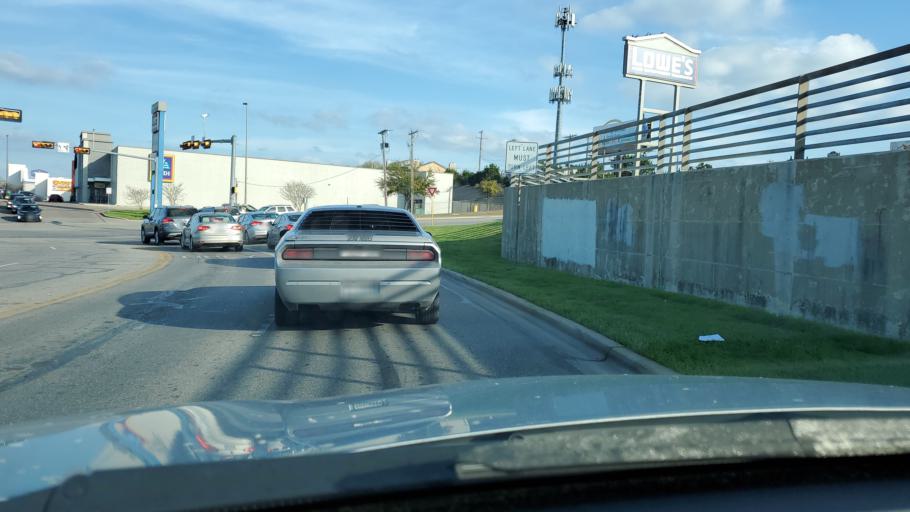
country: US
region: Texas
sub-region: Bell County
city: Killeen
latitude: 31.0884
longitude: -97.7209
